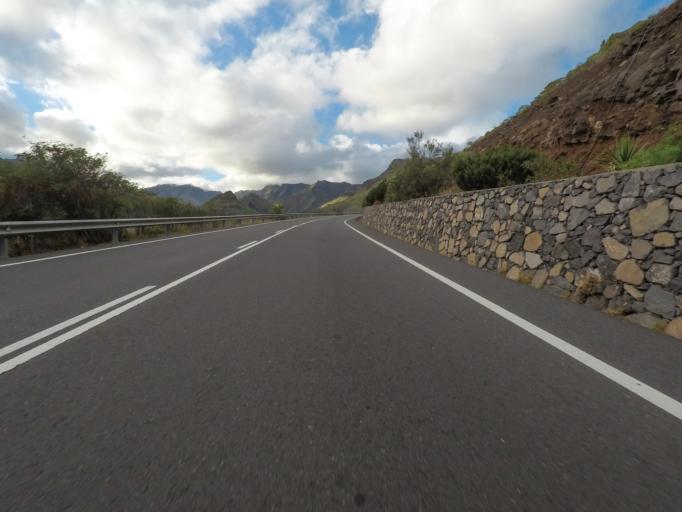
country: ES
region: Canary Islands
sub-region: Provincia de Santa Cruz de Tenerife
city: San Sebastian de la Gomera
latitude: 28.1030
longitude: -17.1223
